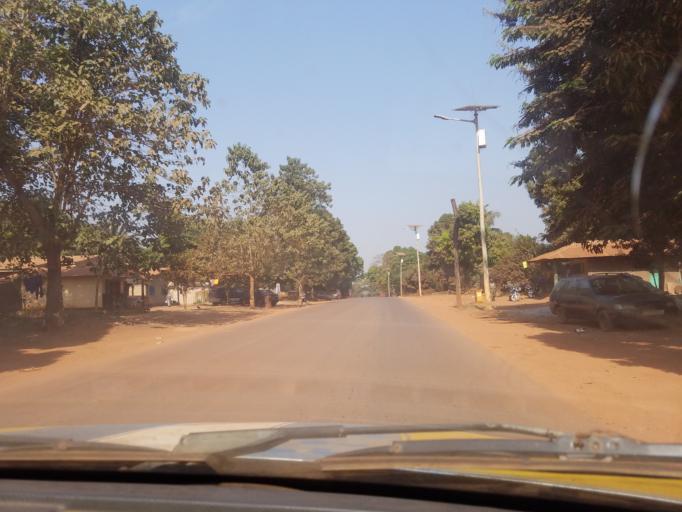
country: GN
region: Boke
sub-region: Boke Prefecture
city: Sangueya
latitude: 10.8061
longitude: -14.3882
